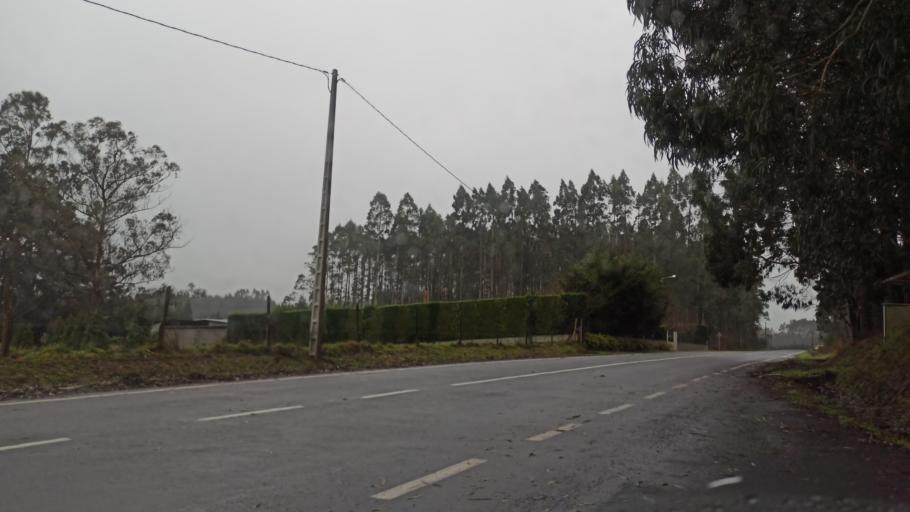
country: ES
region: Galicia
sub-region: Provincia da Coruna
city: Coiros
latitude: 43.1830
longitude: -8.1233
